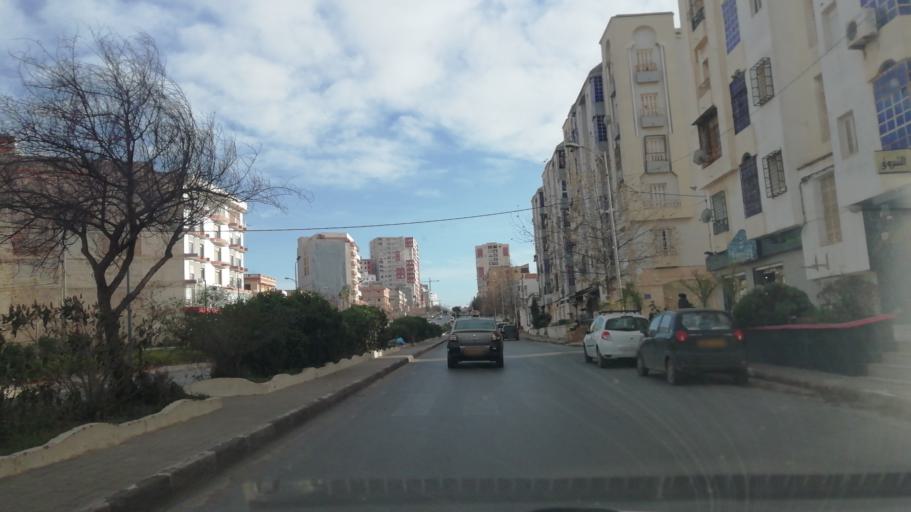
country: DZ
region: Oran
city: Bir el Djir
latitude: 35.7278
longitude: -0.5857
